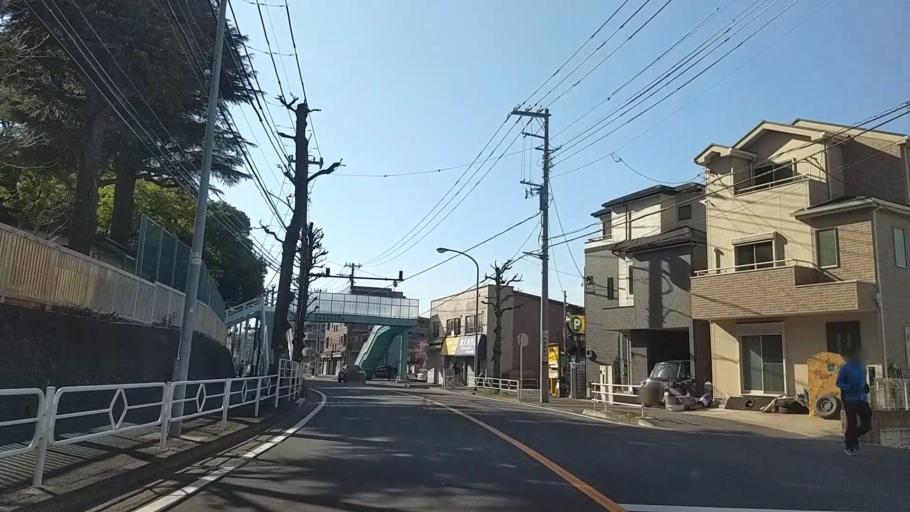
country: JP
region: Kanagawa
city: Yokohama
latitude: 35.3909
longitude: 139.6011
